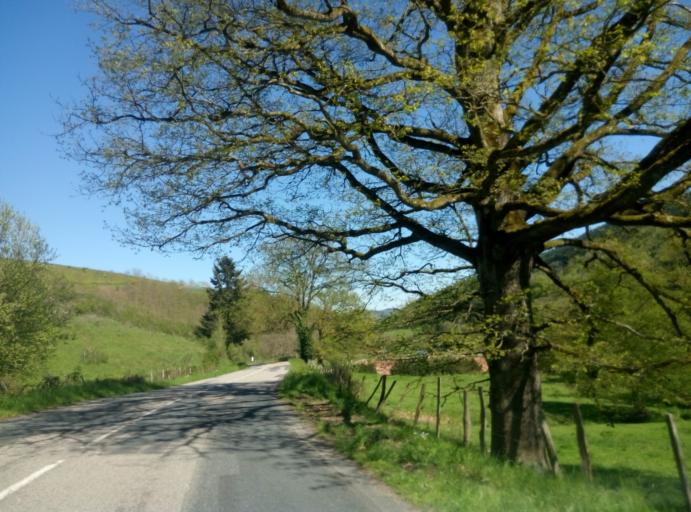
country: FR
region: Rhone-Alpes
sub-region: Departement du Rhone
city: Grandris
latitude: 46.0059
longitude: 4.4544
